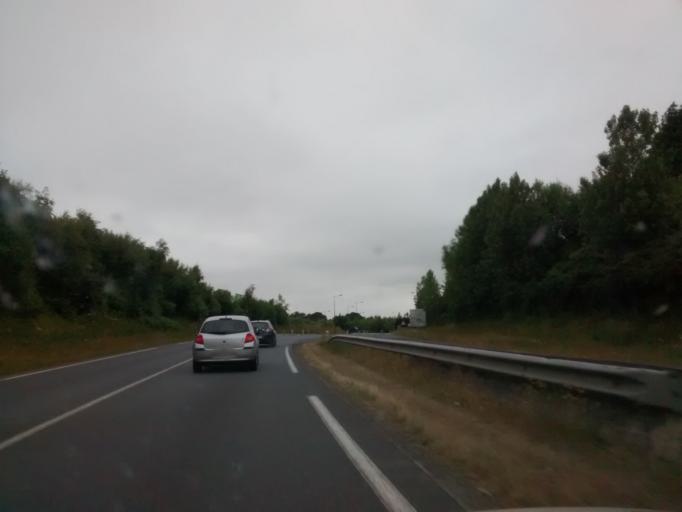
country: FR
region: Brittany
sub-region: Departement des Cotes-d'Armor
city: Lannion
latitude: 48.7489
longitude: -3.4484
